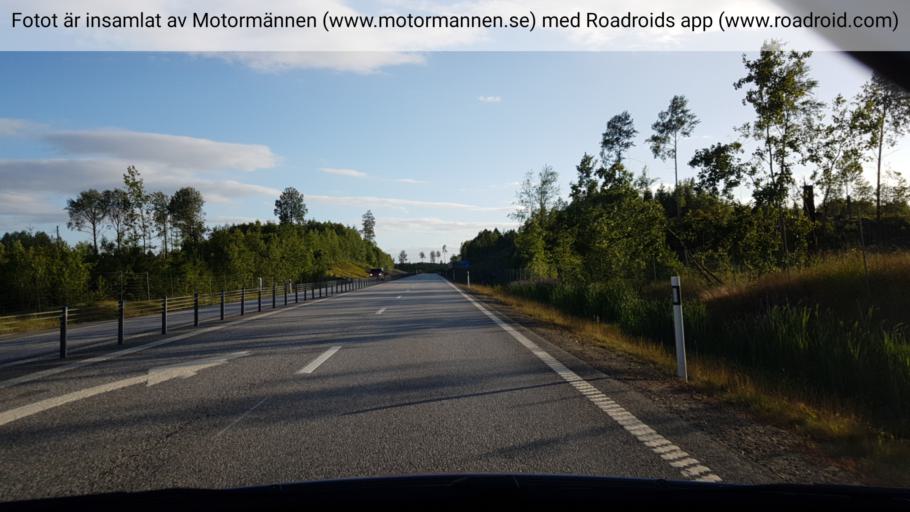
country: SE
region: OErebro
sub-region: Degerfors Kommun
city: Degerfors
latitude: 59.3243
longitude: 14.4200
